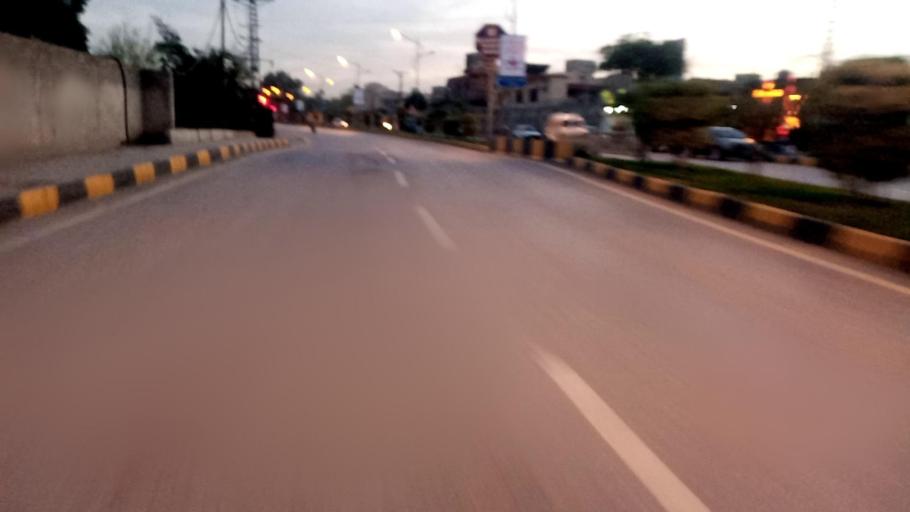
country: PK
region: Khyber Pakhtunkhwa
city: Peshawar
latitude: 34.0163
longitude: 71.5482
